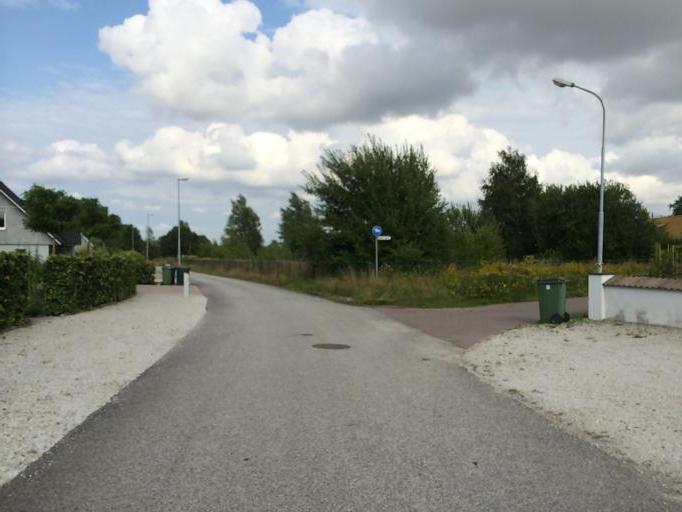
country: SE
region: Skane
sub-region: Lomma Kommun
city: Lomma
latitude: 55.6954
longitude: 13.0588
